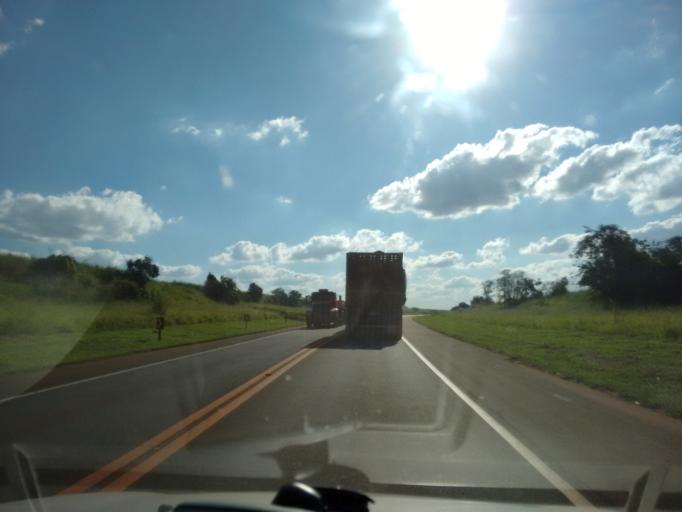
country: BR
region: Sao Paulo
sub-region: Americo Brasiliense
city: Americo Brasiliense
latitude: -21.6210
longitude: -48.0211
